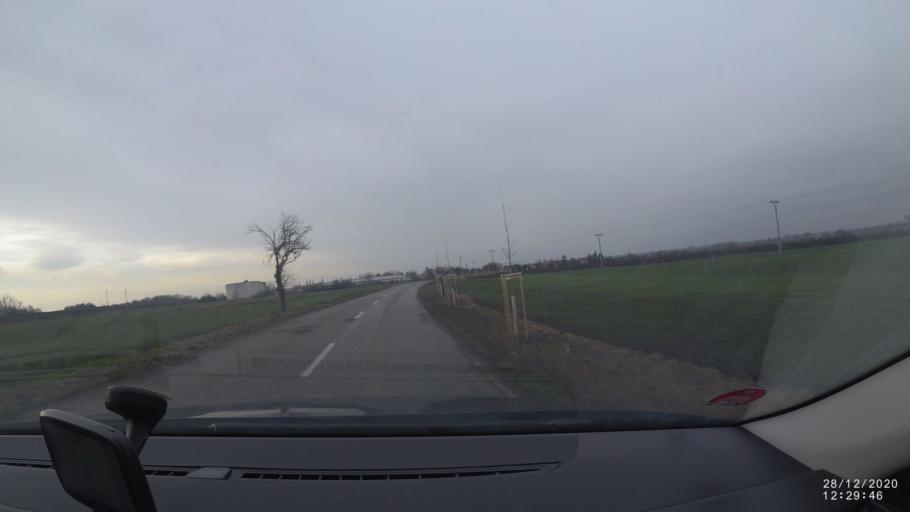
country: CZ
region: Central Bohemia
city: Kostelec nad Labem
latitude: 50.1979
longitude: 14.6069
